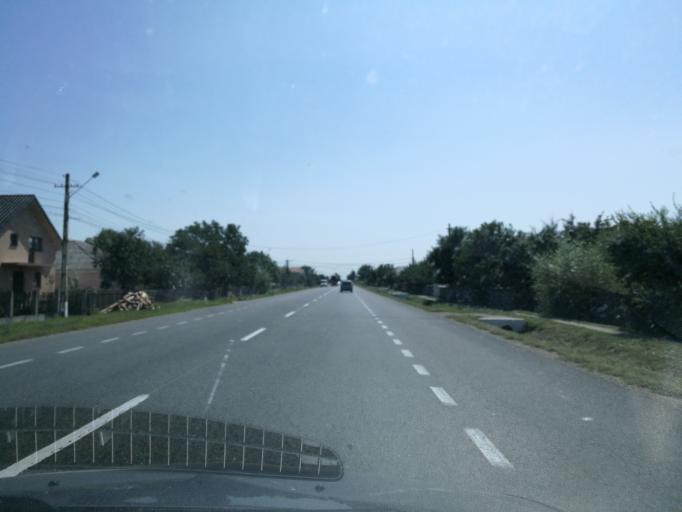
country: RO
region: Bacau
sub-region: Comuna Parava
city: Parava
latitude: 46.3242
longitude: 27.0136
